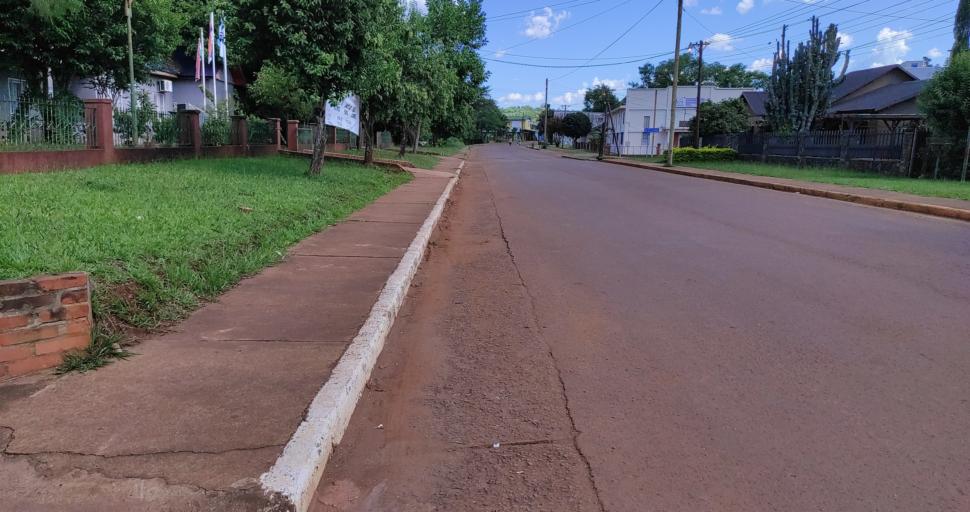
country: AR
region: Misiones
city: El Soberbio
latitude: -27.2985
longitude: -54.1944
